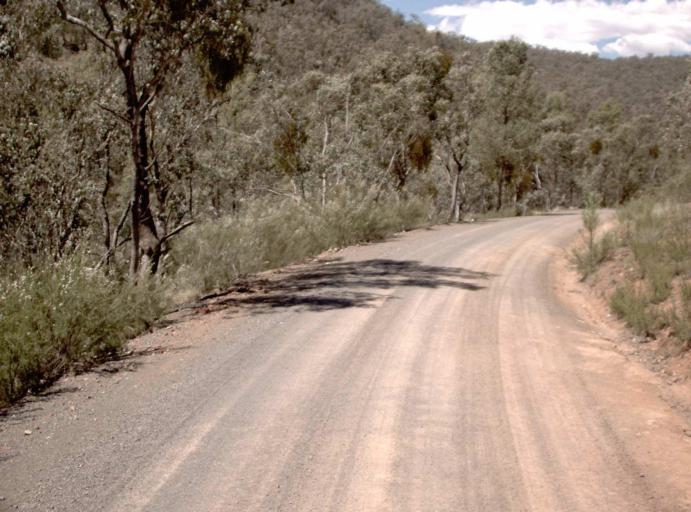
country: AU
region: New South Wales
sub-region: Snowy River
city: Jindabyne
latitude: -37.0629
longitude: 148.5045
